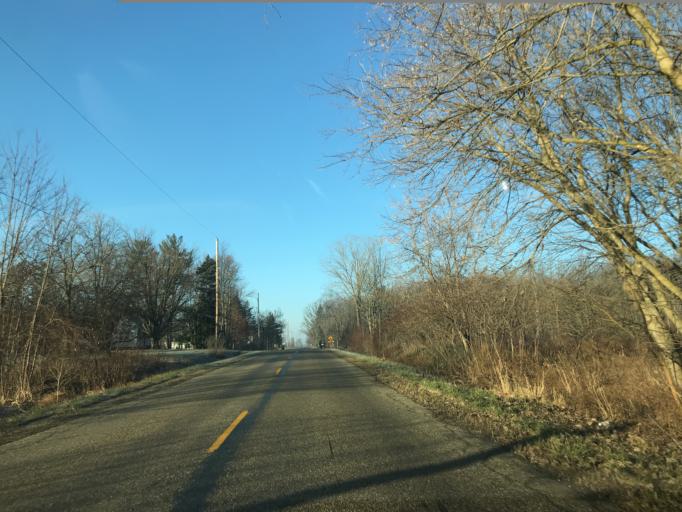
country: US
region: Michigan
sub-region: Eaton County
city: Dimondale
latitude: 42.6620
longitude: -84.6181
